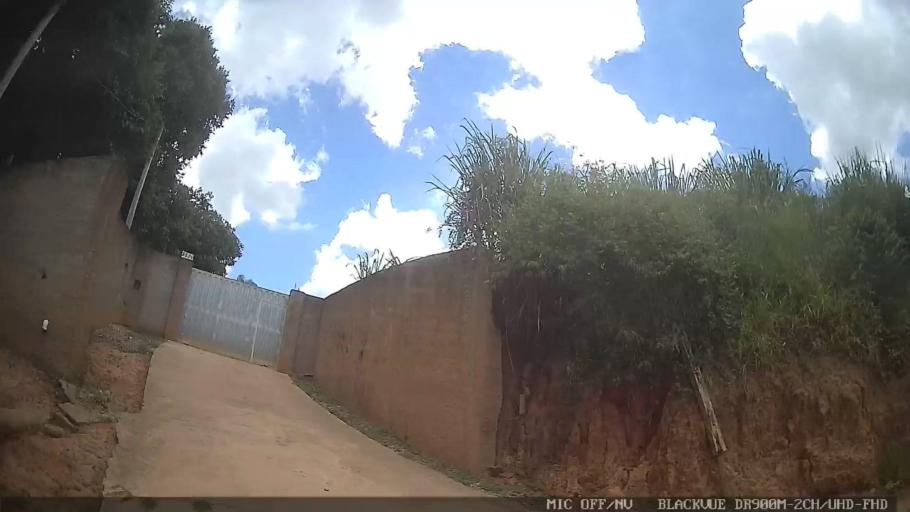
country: BR
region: Sao Paulo
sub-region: Atibaia
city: Atibaia
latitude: -23.1386
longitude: -46.6059
